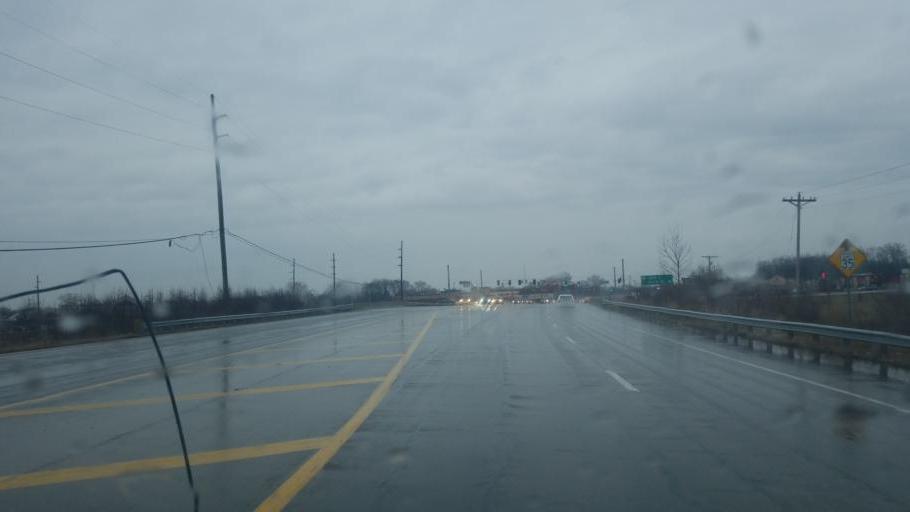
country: US
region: Indiana
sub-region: Bartholomew County
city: Columbus
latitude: 39.2096
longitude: -85.8760
